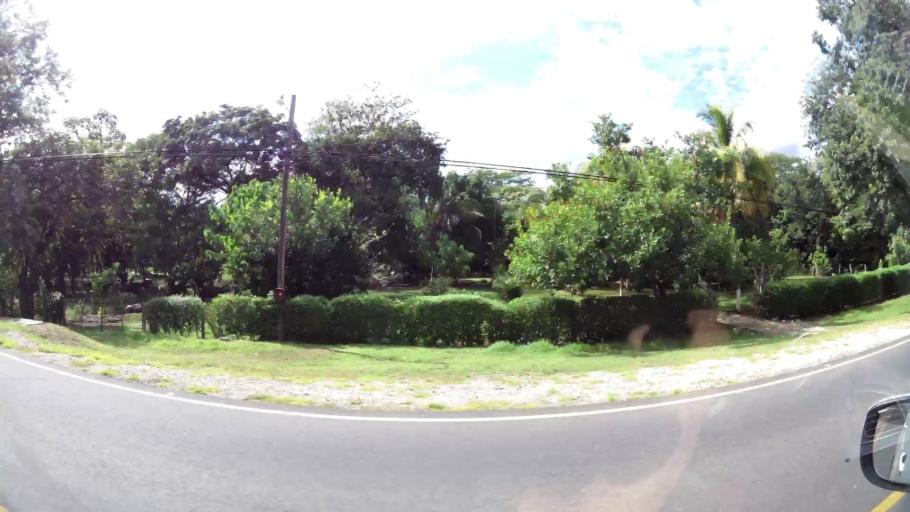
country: CR
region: Guanacaste
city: Hojancha
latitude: 10.1276
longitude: -85.3421
